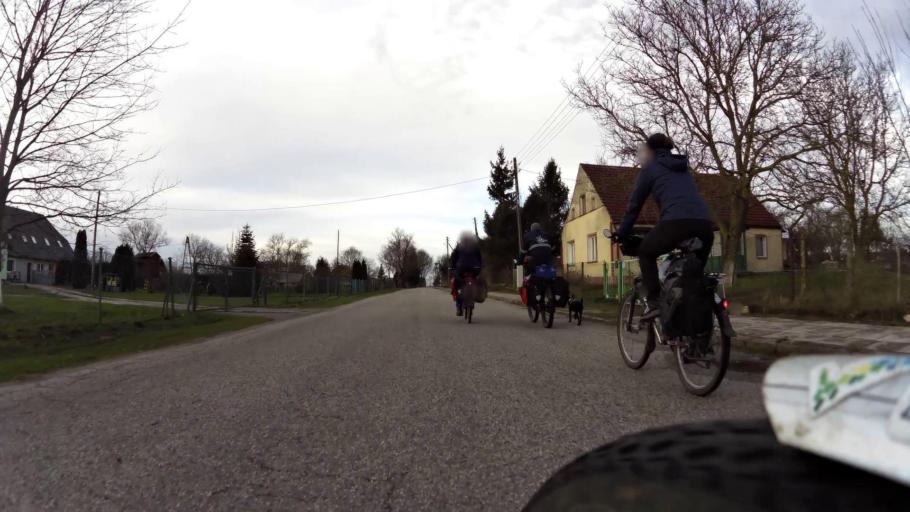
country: PL
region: West Pomeranian Voivodeship
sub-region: Powiat kamienski
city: Kamien Pomorski
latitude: 53.9205
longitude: 14.7594
